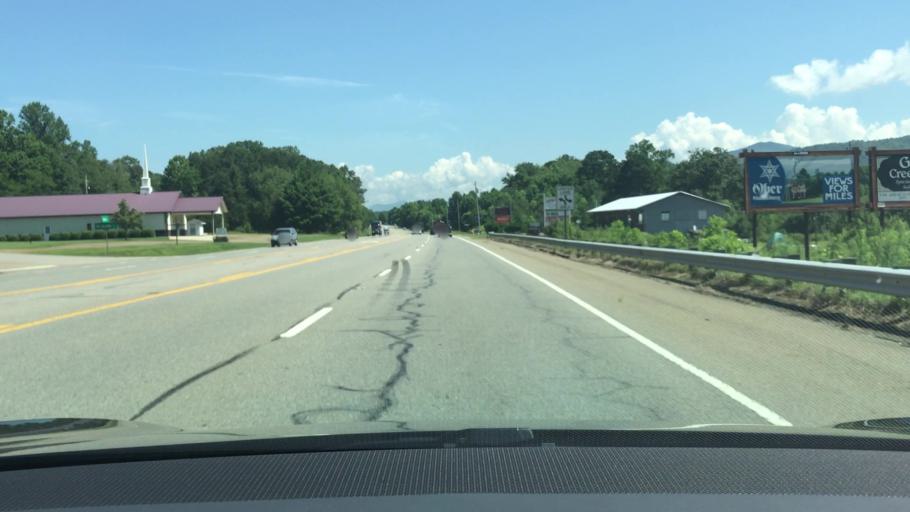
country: US
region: North Carolina
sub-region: Macon County
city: Franklin
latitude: 35.0717
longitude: -83.3868
